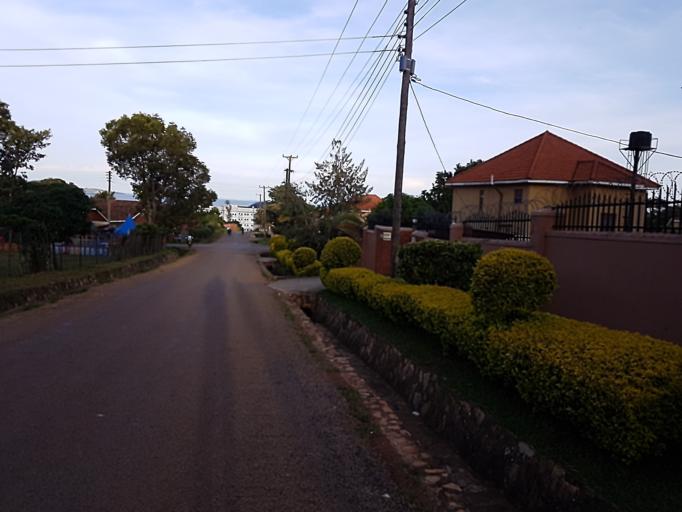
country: UG
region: Central Region
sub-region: Wakiso District
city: Entebbe
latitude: 0.0478
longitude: 32.4671
